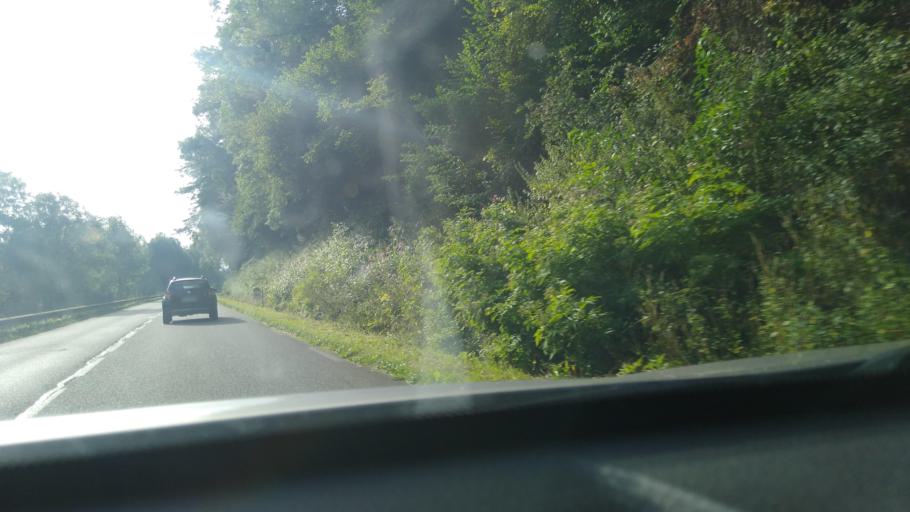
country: FR
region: Midi-Pyrenees
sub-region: Departement de l'Ariege
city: Saint-Lizier
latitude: 43.0336
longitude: 1.0769
